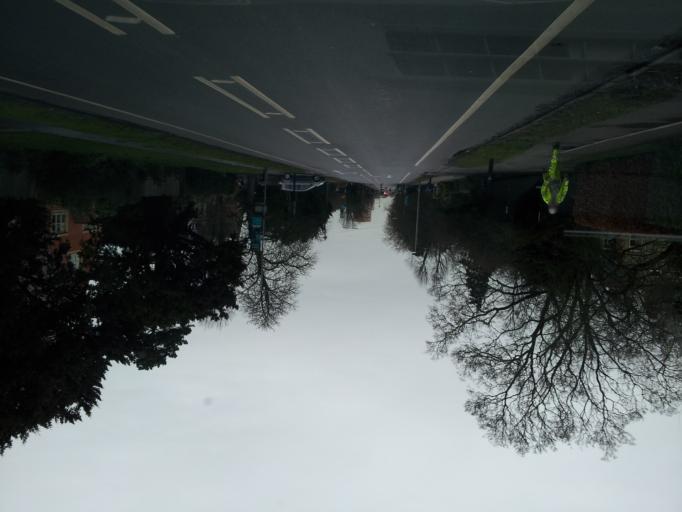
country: GB
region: England
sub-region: Cambridgeshire
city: Cambridge
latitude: 52.1841
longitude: 0.1392
